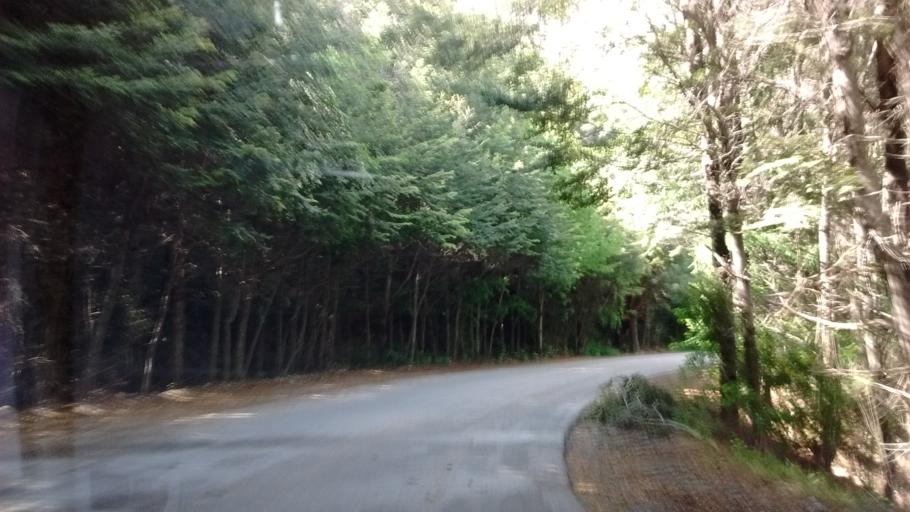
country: AR
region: Rio Negro
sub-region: Departamento de Bariloche
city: San Carlos de Bariloche
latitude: -41.0731
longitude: -71.5447
